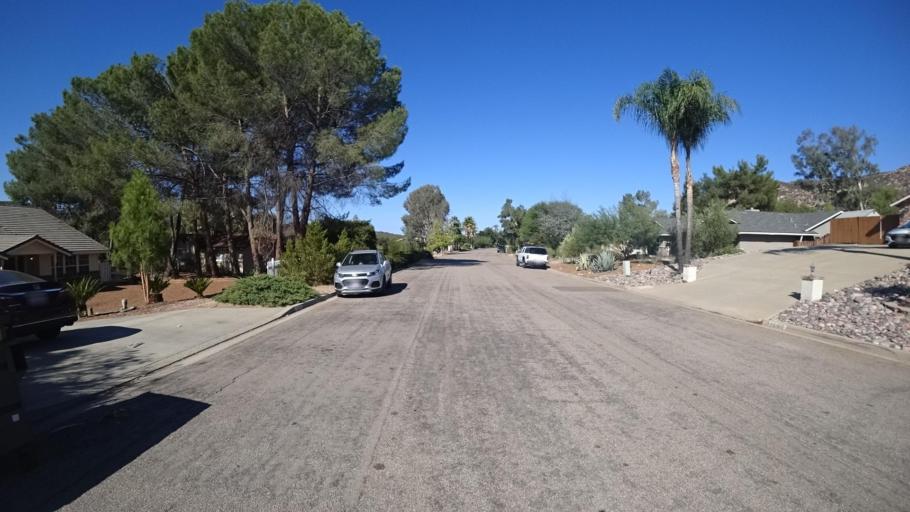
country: US
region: California
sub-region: San Diego County
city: San Diego Country Estates
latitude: 32.9996
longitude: -116.7639
